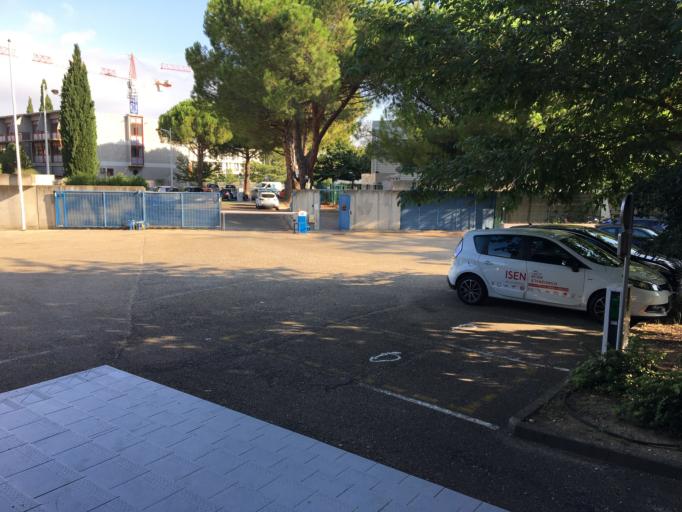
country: FR
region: Languedoc-Roussillon
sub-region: Departement du Gard
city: Nimes
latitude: 43.8212
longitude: 4.3687
